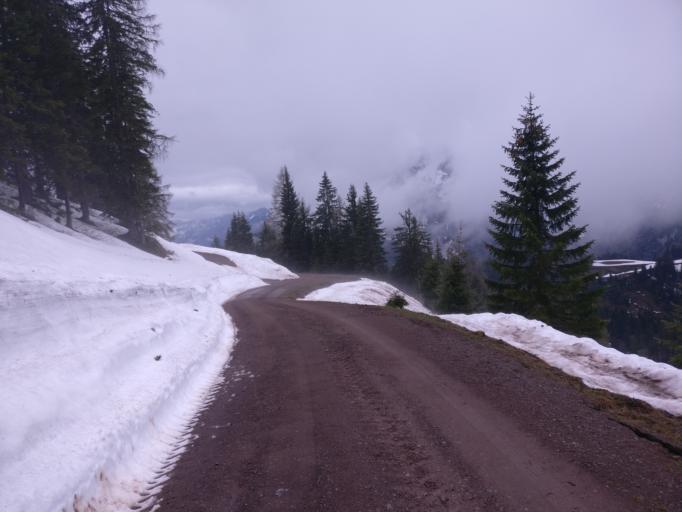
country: AT
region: Salzburg
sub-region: Politischer Bezirk Sankt Johann im Pongau
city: Werfenweng
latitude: 47.4705
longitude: 13.2959
